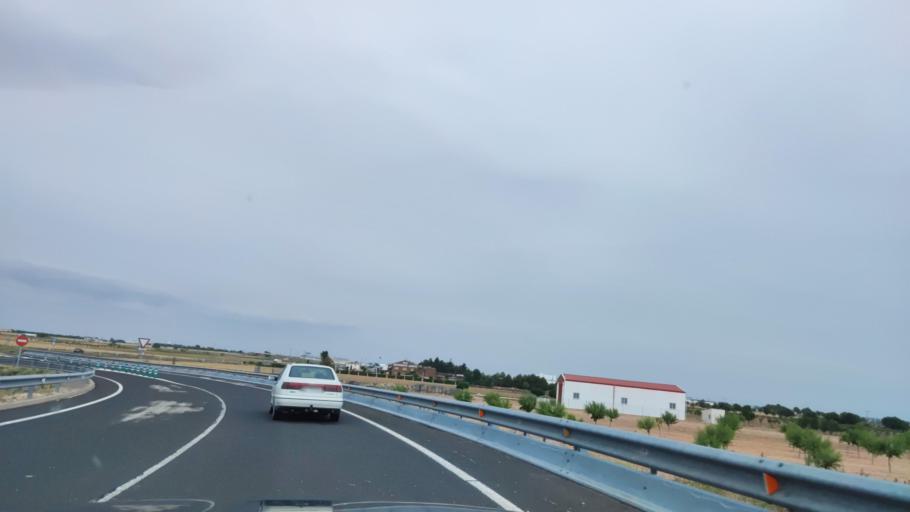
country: ES
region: Castille-La Mancha
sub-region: Provincia de Albacete
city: La Roda
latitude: 39.2191
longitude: -2.1912
